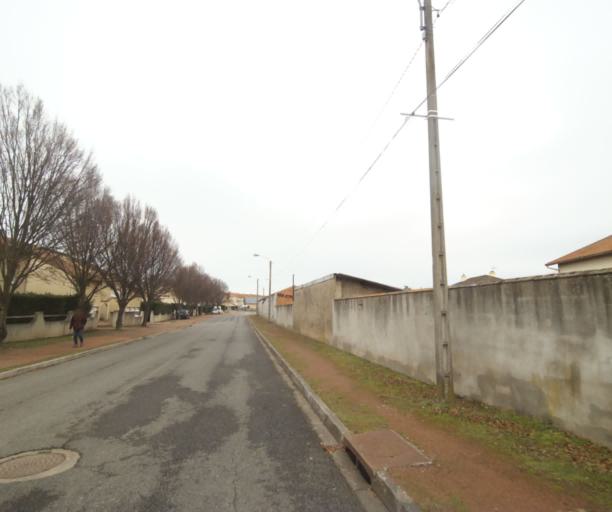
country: FR
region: Rhone-Alpes
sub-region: Departement de la Loire
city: Le Coteau
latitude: 46.0240
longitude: 4.0809
